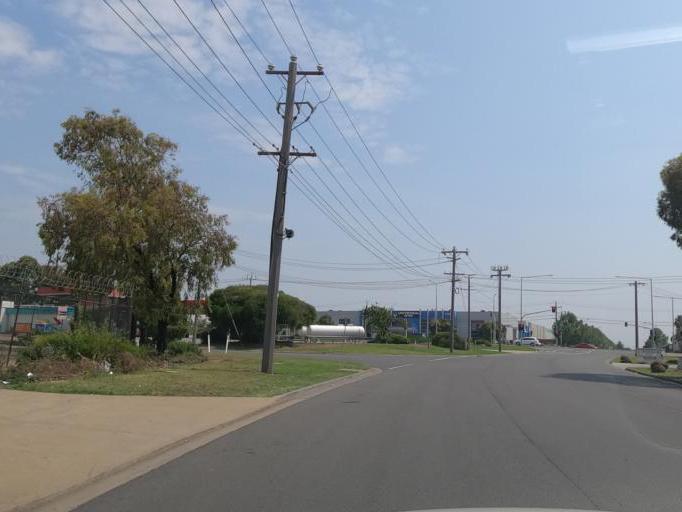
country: AU
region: Victoria
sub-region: Hume
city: Coolaroo
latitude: -37.6440
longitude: 144.9466
